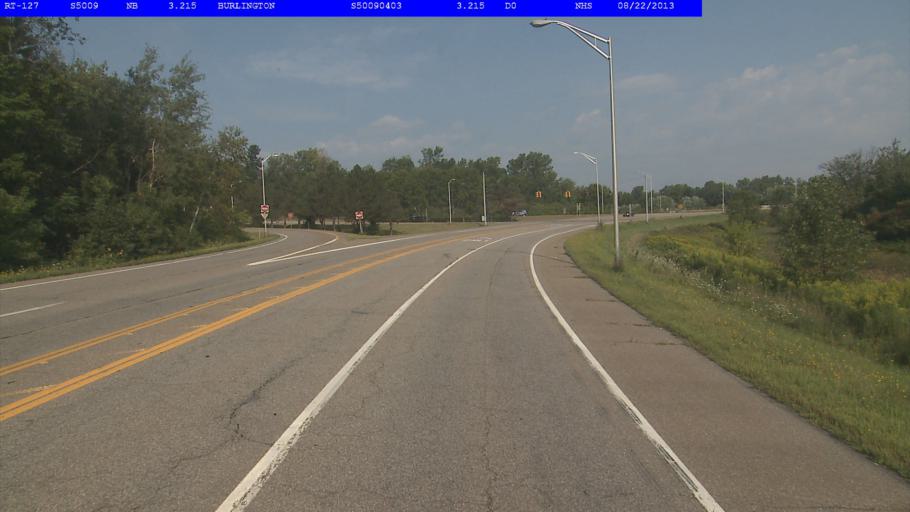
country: US
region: Vermont
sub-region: Chittenden County
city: Burlington
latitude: 44.5221
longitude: -73.2541
